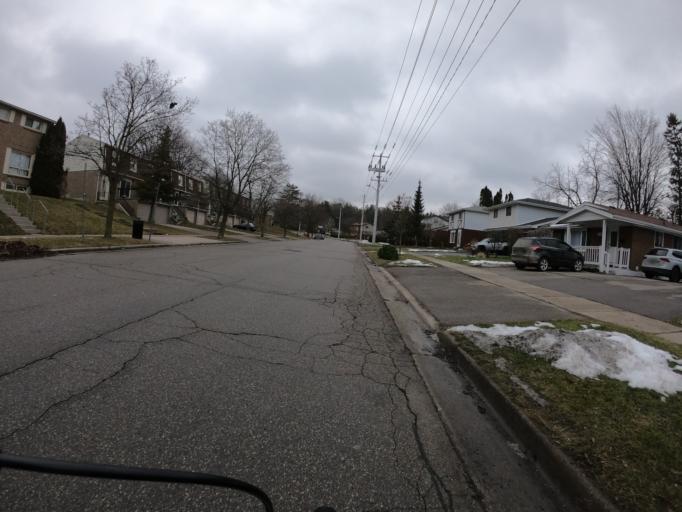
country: CA
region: Ontario
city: Kitchener
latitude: 43.3955
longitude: -80.4285
